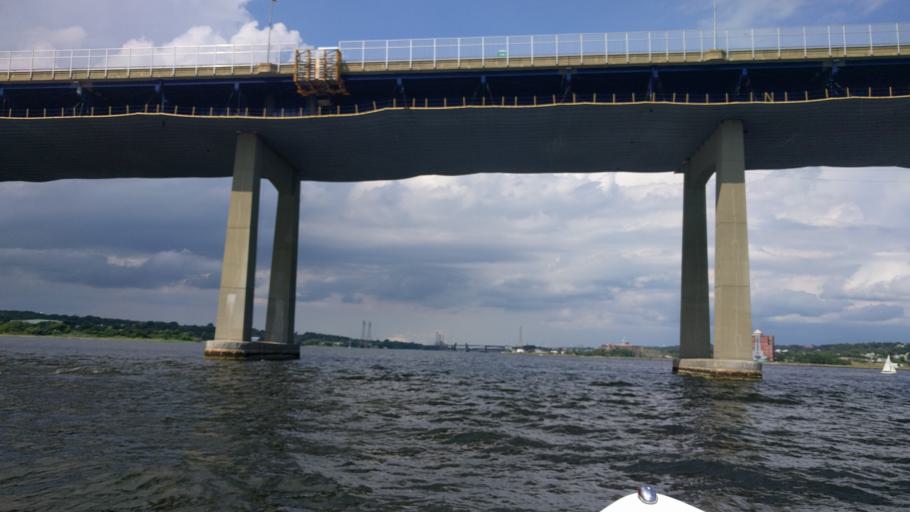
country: US
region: Massachusetts
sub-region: Bristol County
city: Fall River
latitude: 41.7077
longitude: -71.1696
